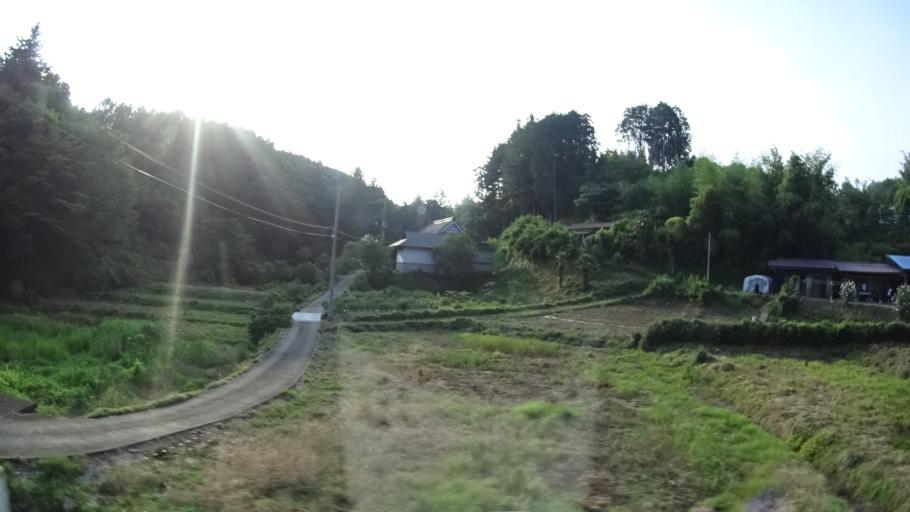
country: JP
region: Tochigi
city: Karasuyama
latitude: 36.6047
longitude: 140.1512
